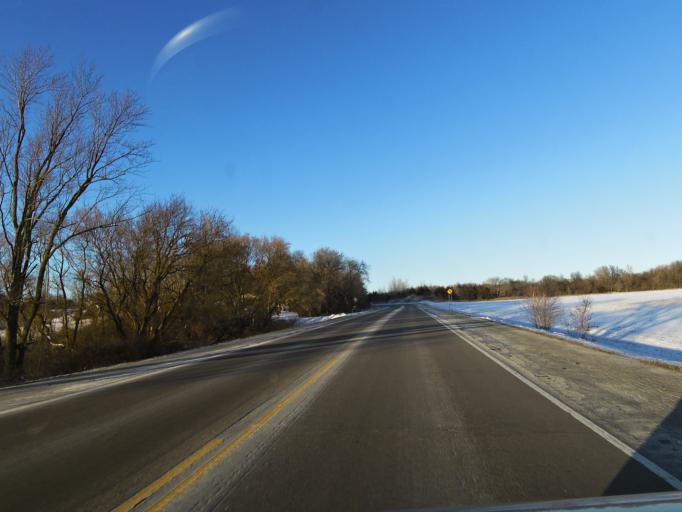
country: US
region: Minnesota
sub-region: Dakota County
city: Farmington
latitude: 44.5562
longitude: -93.1365
